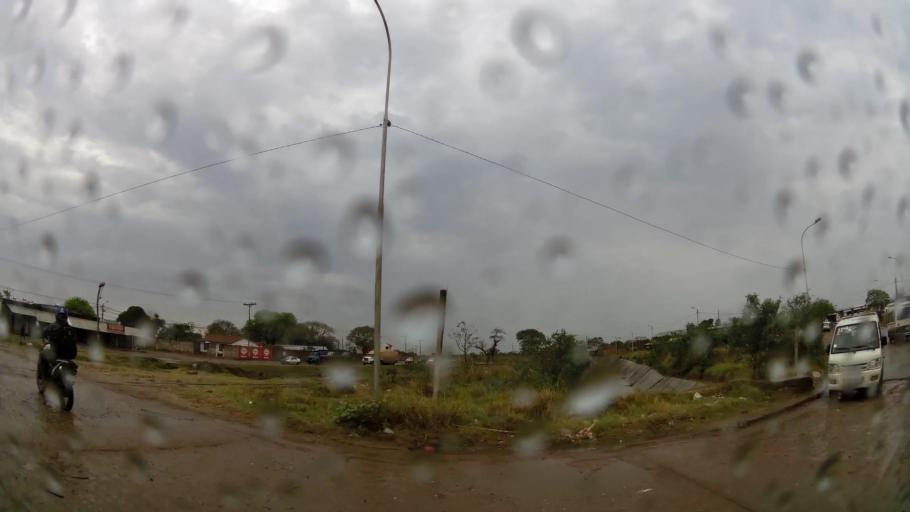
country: BO
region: Santa Cruz
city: Santa Cruz de la Sierra
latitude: -17.7551
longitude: -63.1314
